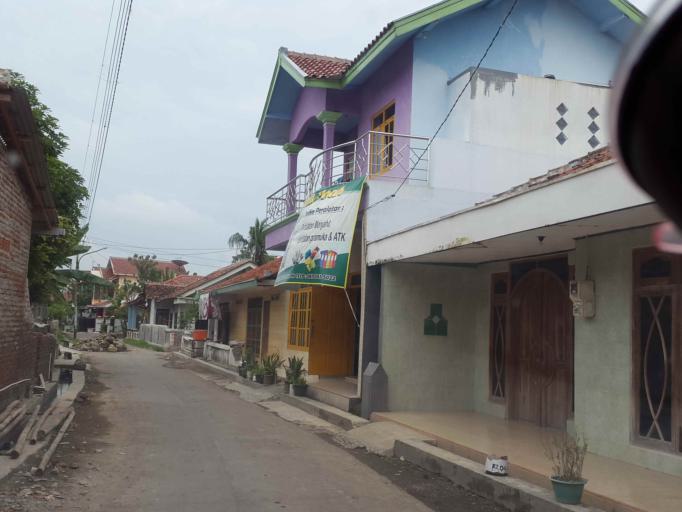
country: ID
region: Central Java
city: Dukuhturi
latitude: -6.8784
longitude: 109.1007
